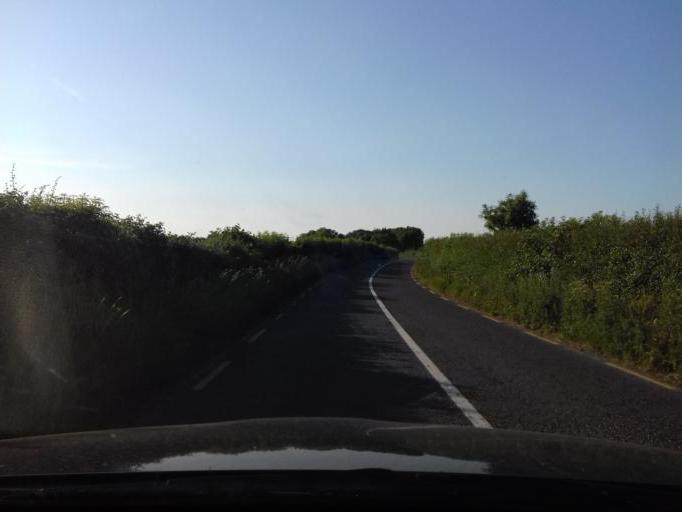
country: IE
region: Leinster
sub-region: An Mhi
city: Ashbourne
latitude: 53.5350
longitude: -6.3656
